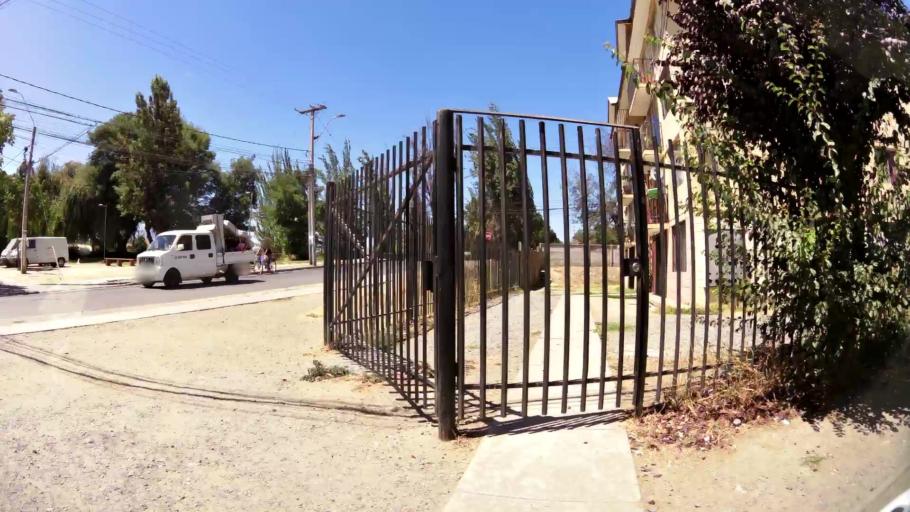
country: CL
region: O'Higgins
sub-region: Provincia de Cachapoal
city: Rancagua
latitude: -34.1575
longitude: -70.7533
